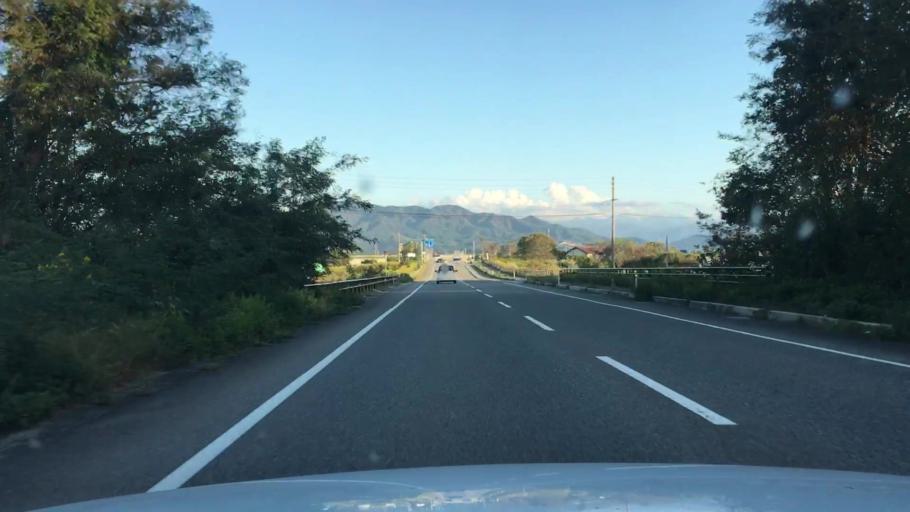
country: JP
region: Niigata
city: Murakami
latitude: 38.1231
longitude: 139.4055
